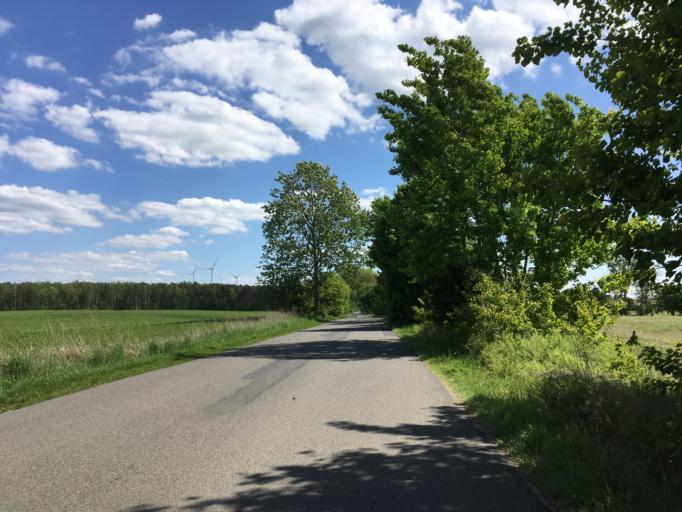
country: DE
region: Brandenburg
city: Rudnitz
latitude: 52.7025
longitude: 13.6635
